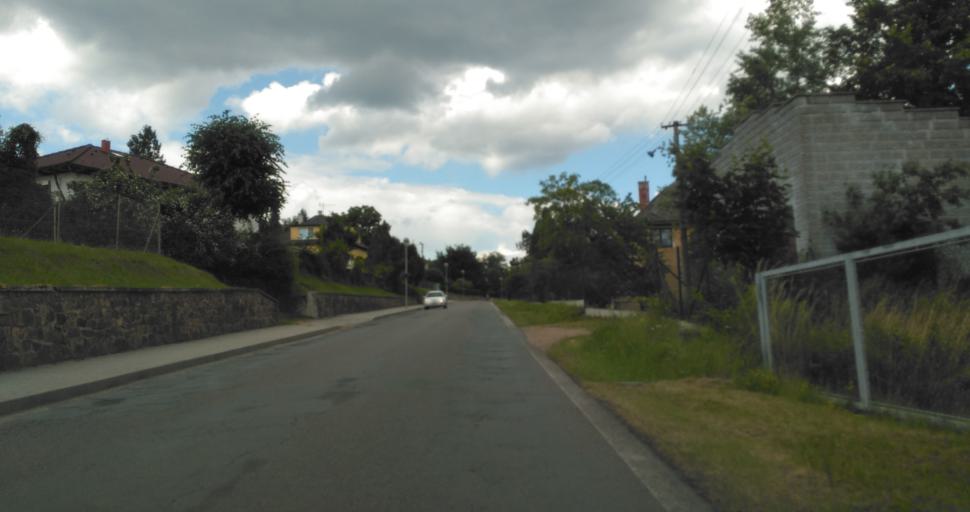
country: CZ
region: Plzensky
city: Zbiroh
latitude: 49.8534
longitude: 13.7680
